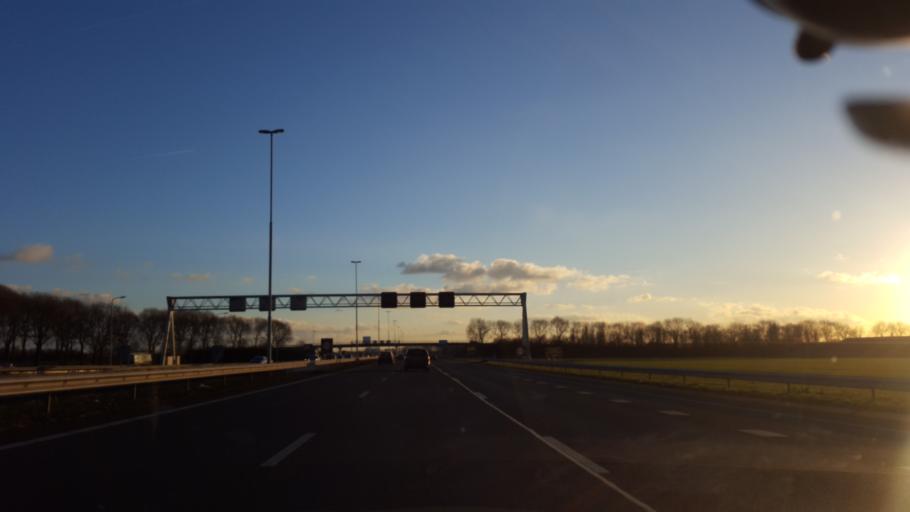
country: NL
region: Gelderland
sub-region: Gemeente Zaltbommel
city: Zaltbommel
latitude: 51.7914
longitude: 5.2578
